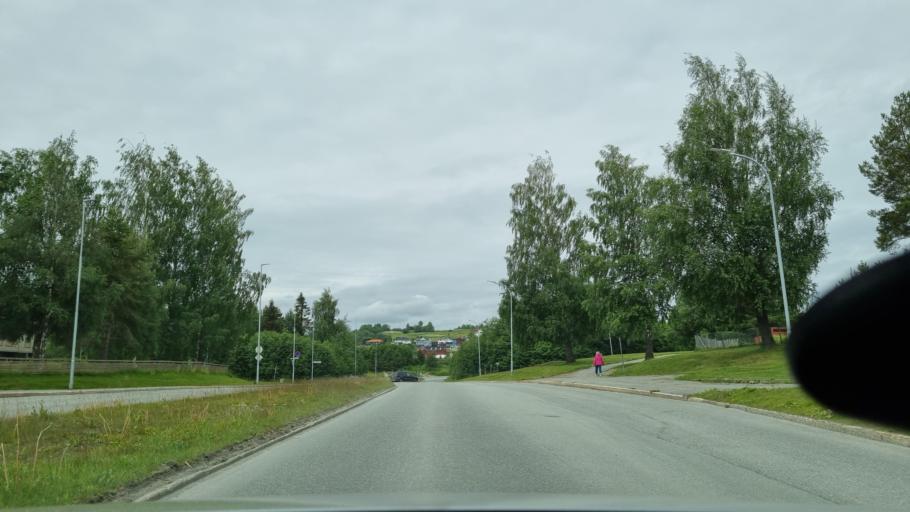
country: NO
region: Sor-Trondelag
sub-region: Melhus
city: Melhus
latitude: 63.3470
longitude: 10.3326
